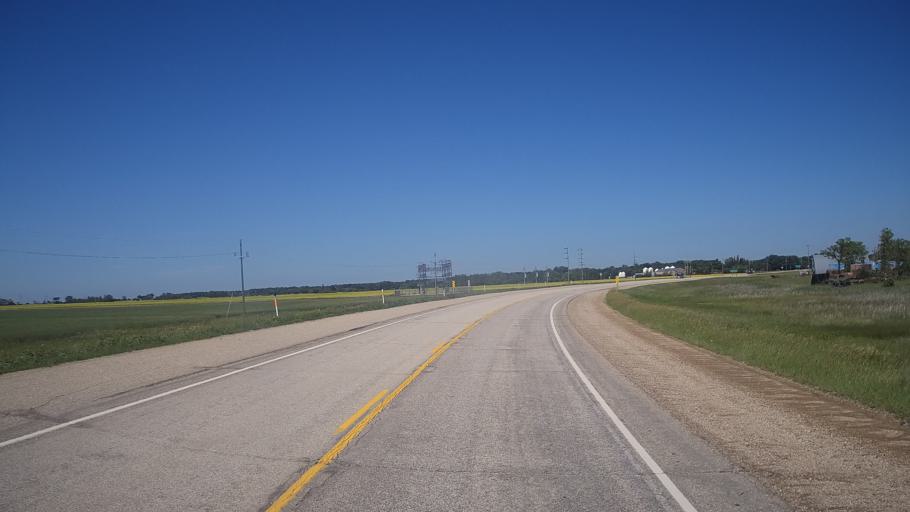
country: CA
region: Manitoba
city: Portage la Prairie
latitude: 50.1264
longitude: -98.5787
